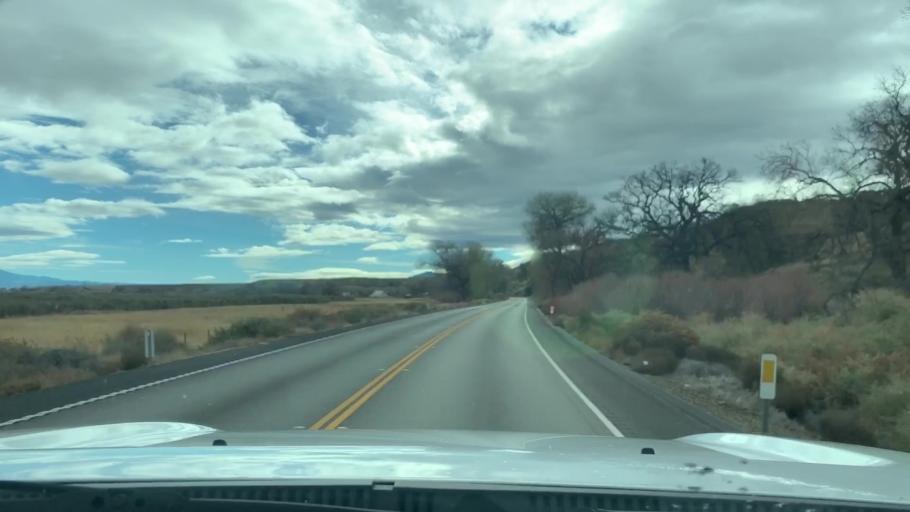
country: US
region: California
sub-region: Kern County
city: Taft Heights
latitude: 34.9930
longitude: -119.8030
